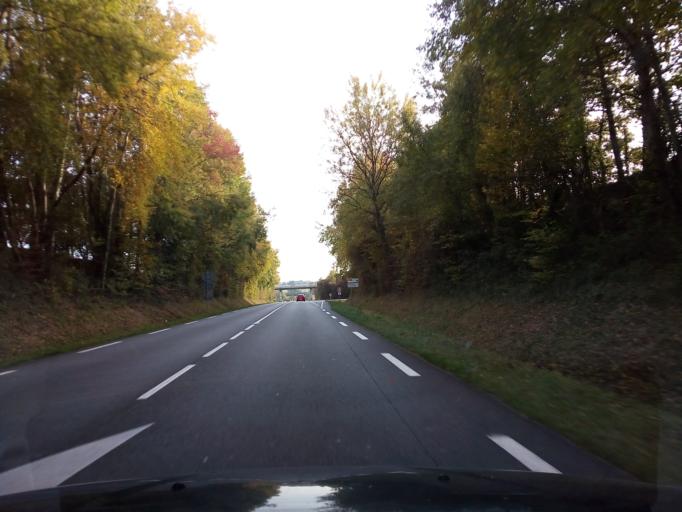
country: FR
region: Poitou-Charentes
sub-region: Departement de la Charente
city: Confolens
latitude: 46.0533
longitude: 0.6667
